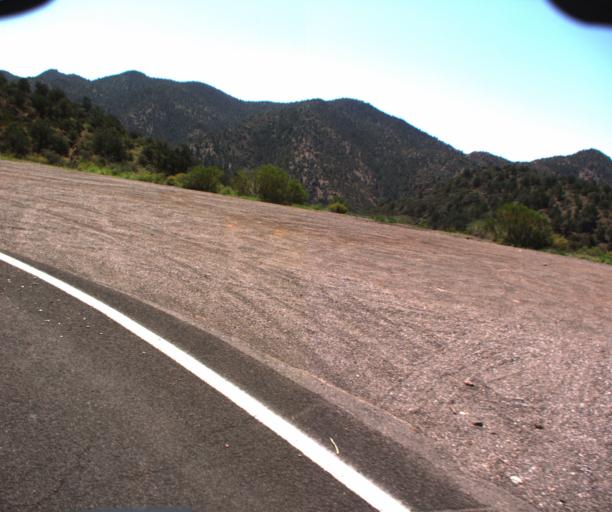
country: US
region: Arizona
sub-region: Greenlee County
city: Morenci
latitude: 33.1630
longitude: -109.3680
